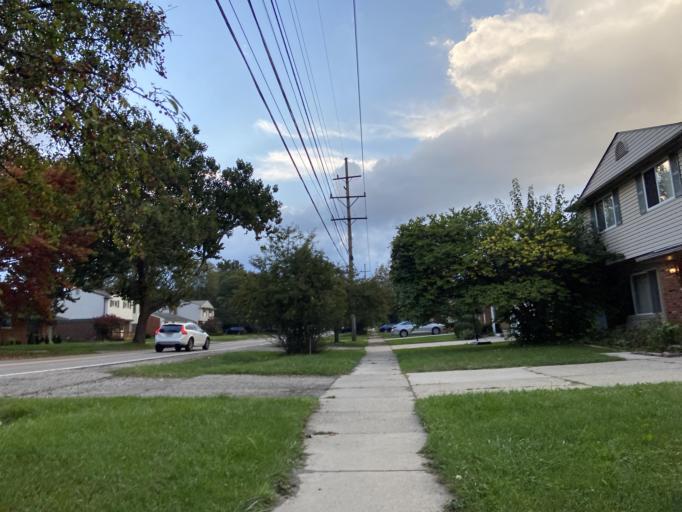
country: US
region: Michigan
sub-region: Oakland County
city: Farmington
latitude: 42.4574
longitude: -83.3442
